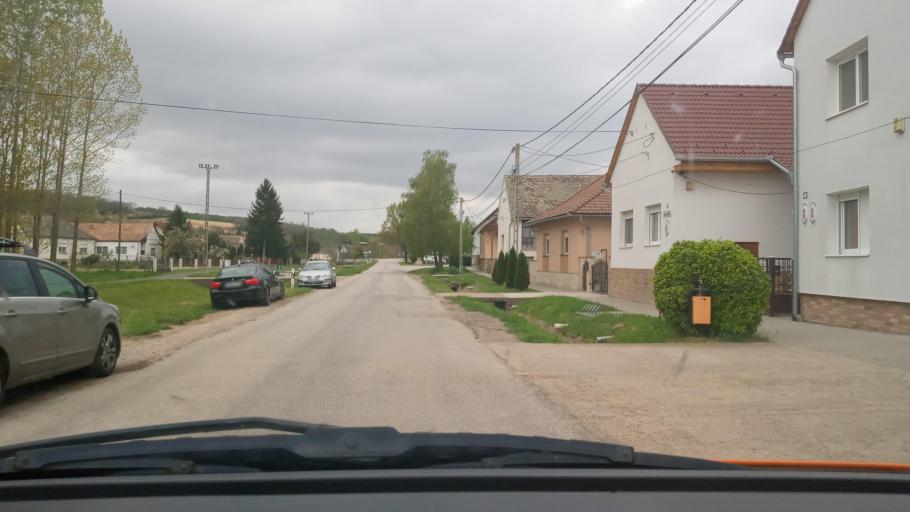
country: HU
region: Baranya
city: Boly
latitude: 46.0044
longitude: 18.5518
